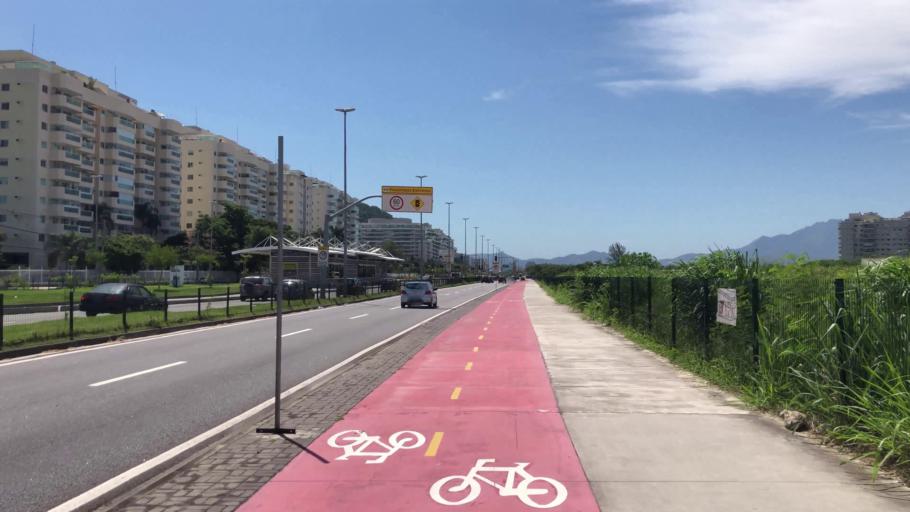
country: BR
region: Rio de Janeiro
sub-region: Nilopolis
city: Nilopolis
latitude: -22.9733
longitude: -43.3939
